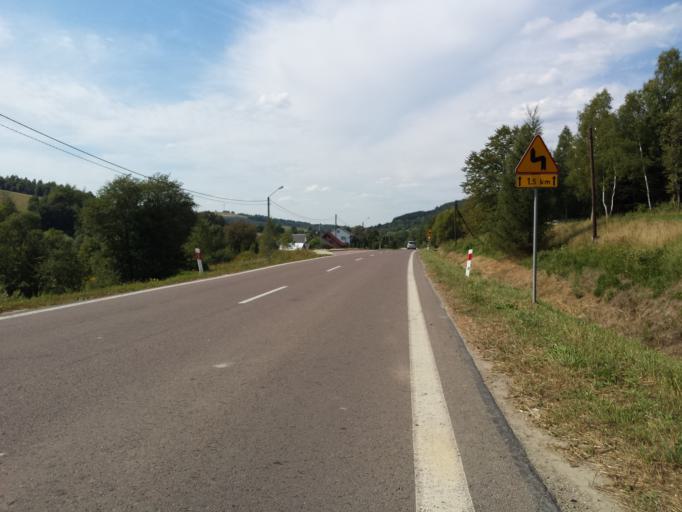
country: PL
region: Subcarpathian Voivodeship
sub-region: Powiat bieszczadzki
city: Ustrzyki Dolne
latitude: 49.5484
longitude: 22.5800
